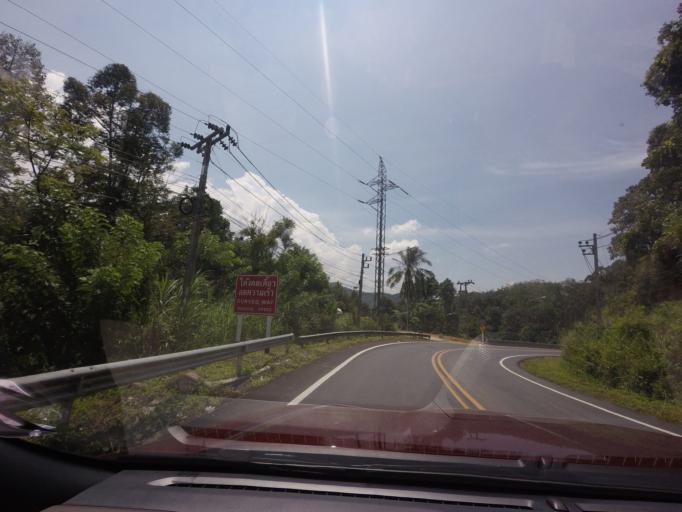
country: TH
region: Yala
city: Betong
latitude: 5.9030
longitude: 101.1470
